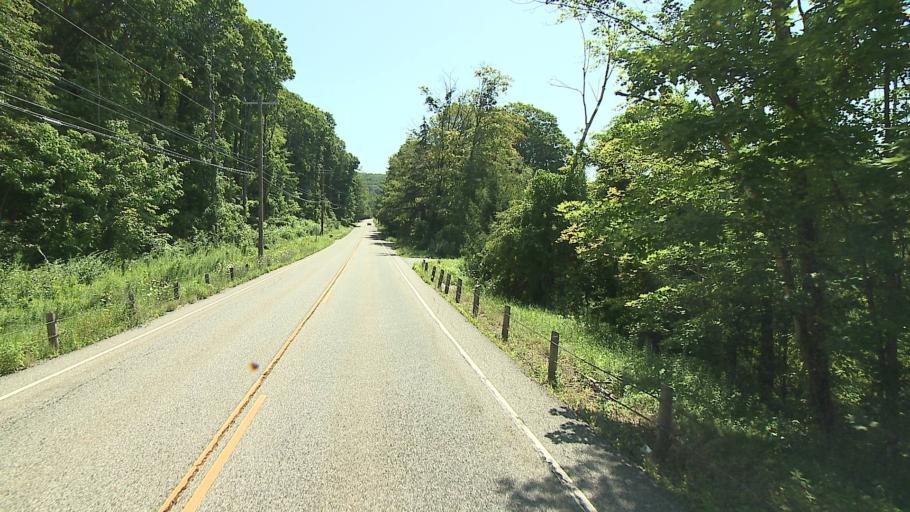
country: US
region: Connecticut
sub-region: Litchfield County
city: Kent
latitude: 41.8540
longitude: -73.4462
